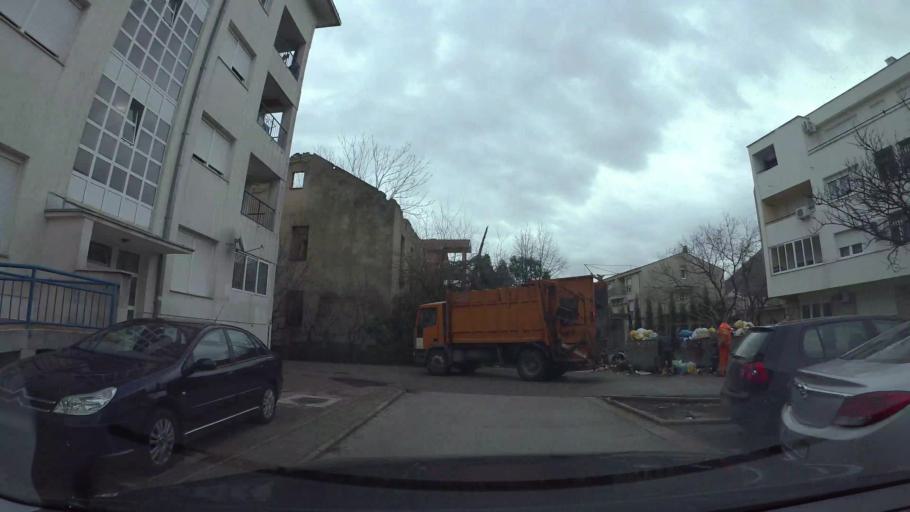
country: BA
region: Federation of Bosnia and Herzegovina
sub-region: Hercegovacko-Bosanski Kanton
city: Mostar
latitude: 43.3402
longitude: 17.8075
